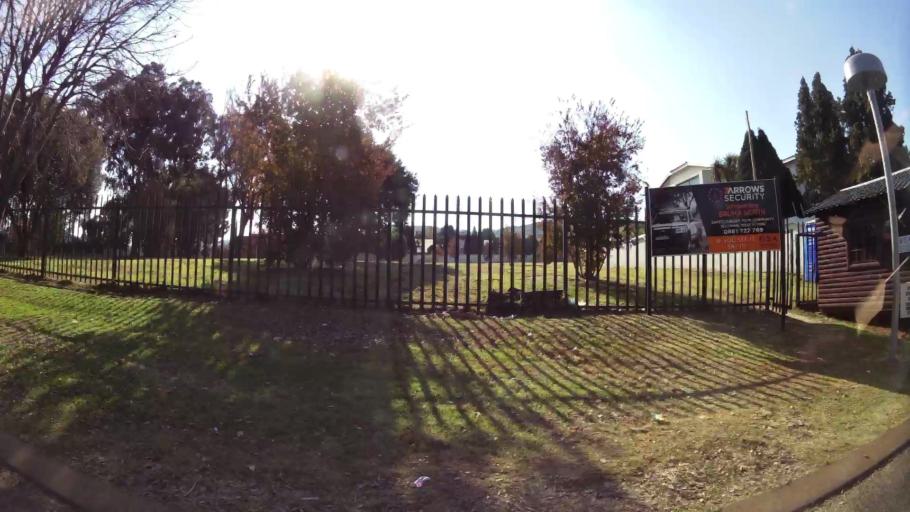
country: ZA
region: Gauteng
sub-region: City of Johannesburg Metropolitan Municipality
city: Johannesburg
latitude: -26.1758
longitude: 28.1092
